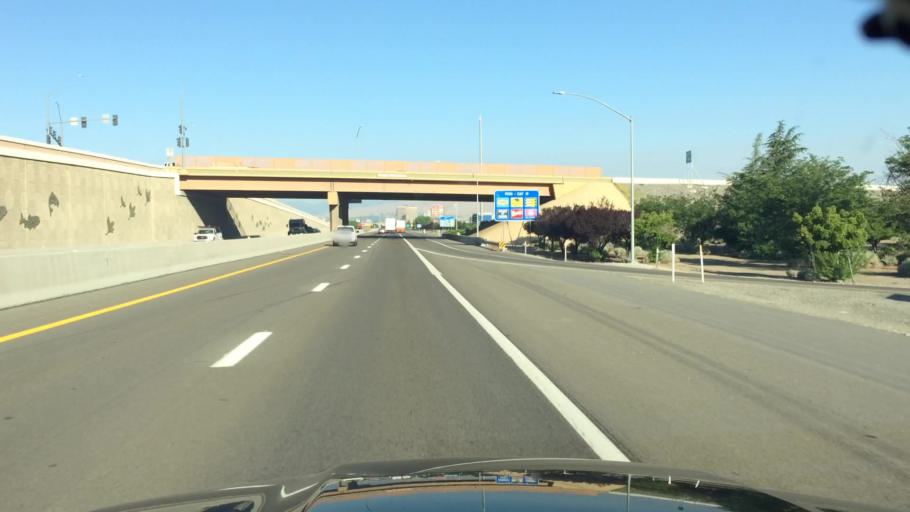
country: US
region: Nevada
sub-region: Washoe County
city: Sparks
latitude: 39.5281
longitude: -119.7136
